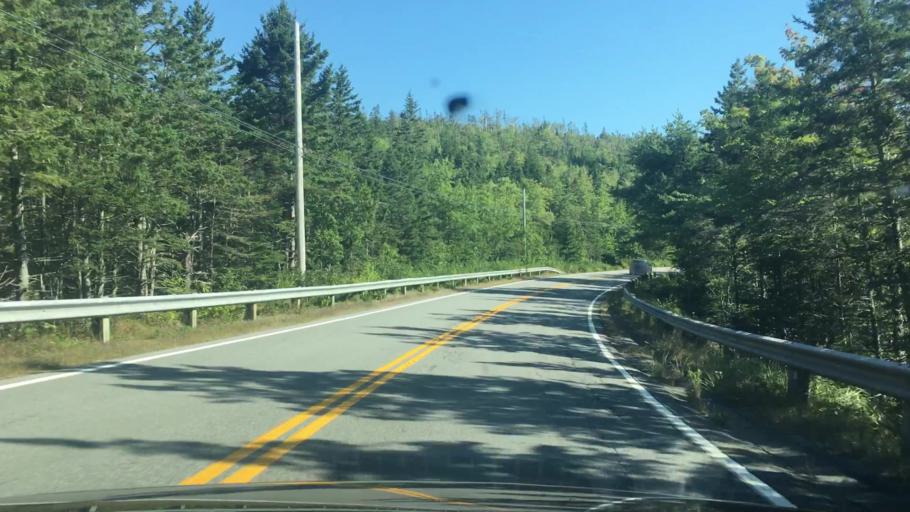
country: CA
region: Nova Scotia
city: Cole Harbour
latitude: 44.8156
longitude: -62.8849
